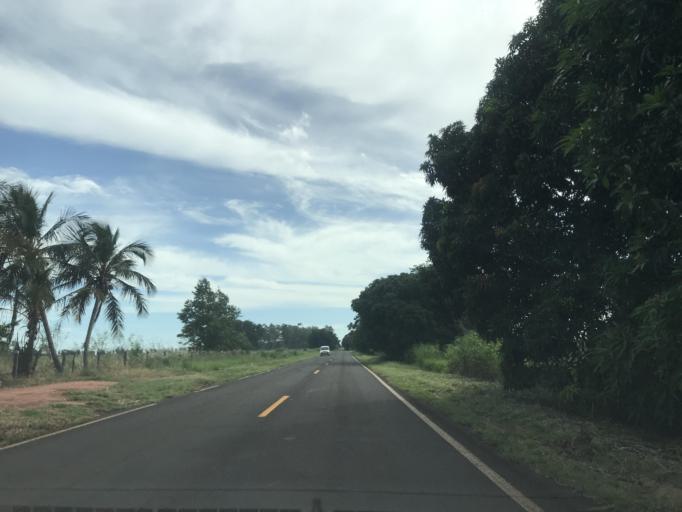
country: BR
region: Parana
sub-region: Terra Rica
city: Terra Rica
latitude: -22.7665
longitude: -52.6405
